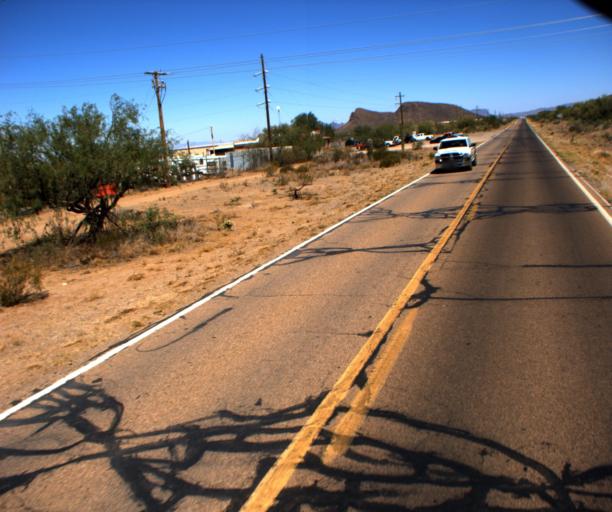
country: US
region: Arizona
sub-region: Pima County
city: Sells
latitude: 31.9350
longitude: -111.9136
